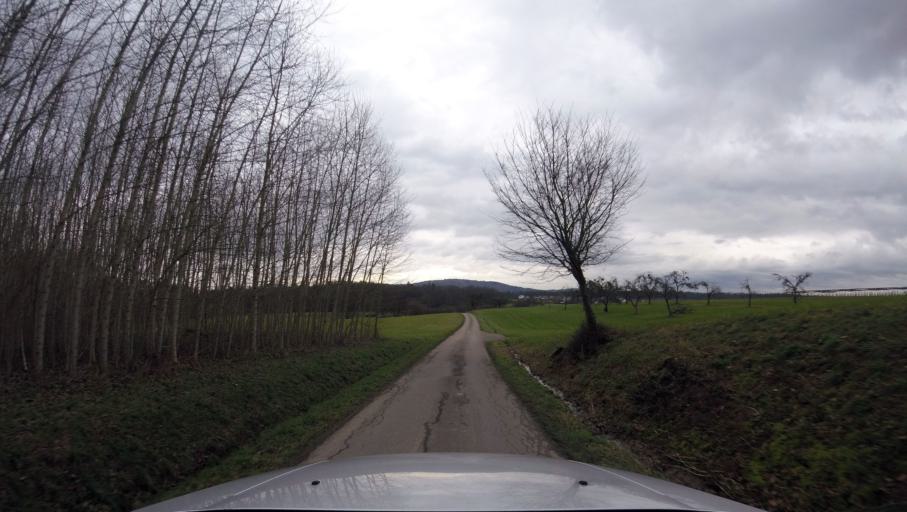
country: DE
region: Baden-Wuerttemberg
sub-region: Regierungsbezirk Stuttgart
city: Oppenweiler
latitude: 48.9781
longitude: 9.4303
